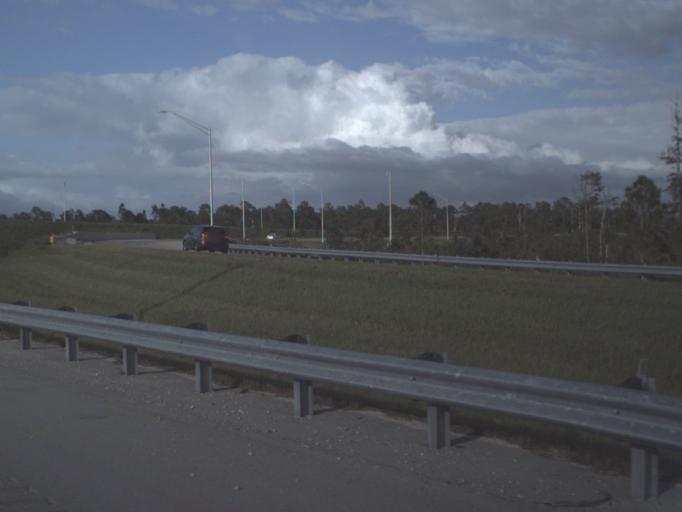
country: US
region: Florida
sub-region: Lee County
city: Three Oaks
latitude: 26.5095
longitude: -81.7941
